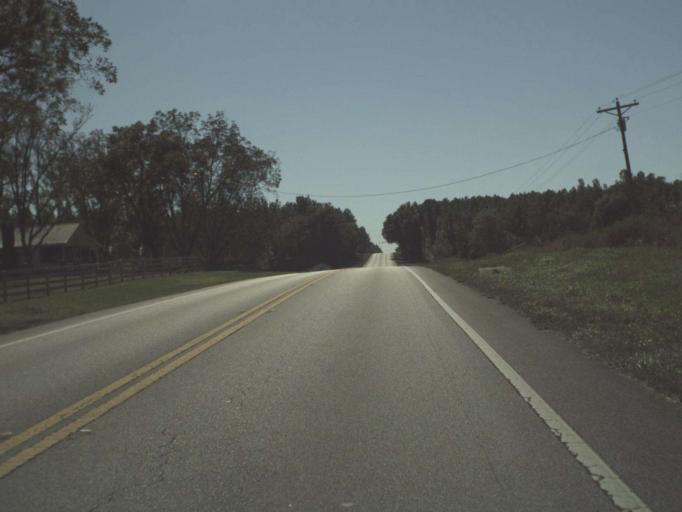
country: US
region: Florida
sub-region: Walton County
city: DeFuniak Springs
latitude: 30.9124
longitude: -86.1337
